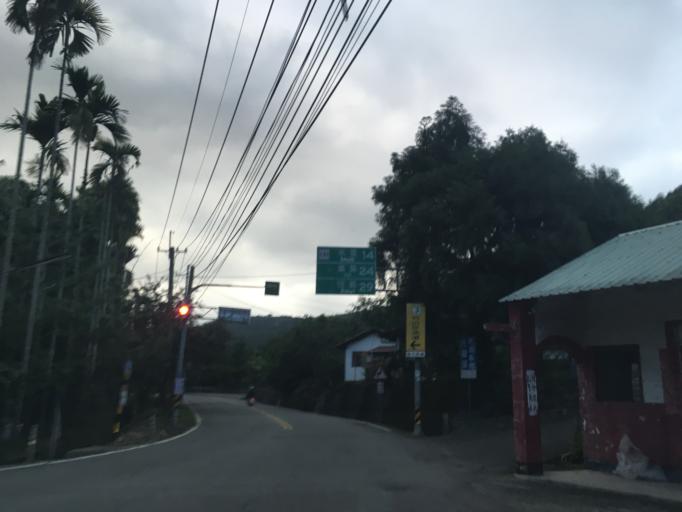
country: TW
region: Taiwan
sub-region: Nantou
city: Puli
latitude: 23.9052
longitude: 120.9214
